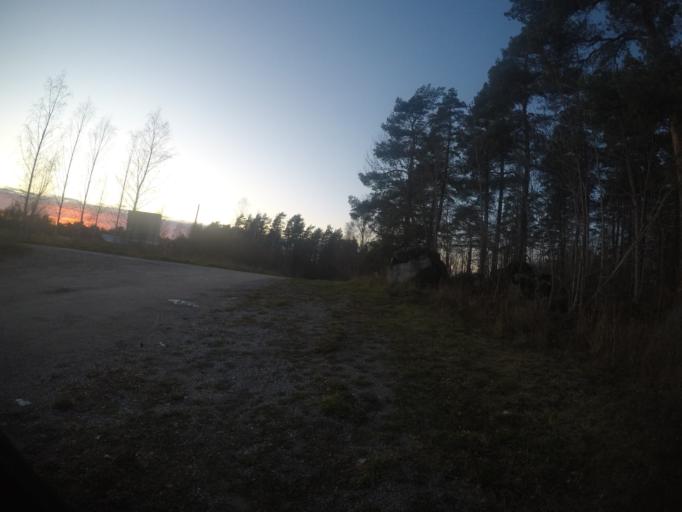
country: SE
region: OErebro
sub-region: Lindesbergs Kommun
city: Frovi
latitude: 59.3192
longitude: 15.4158
